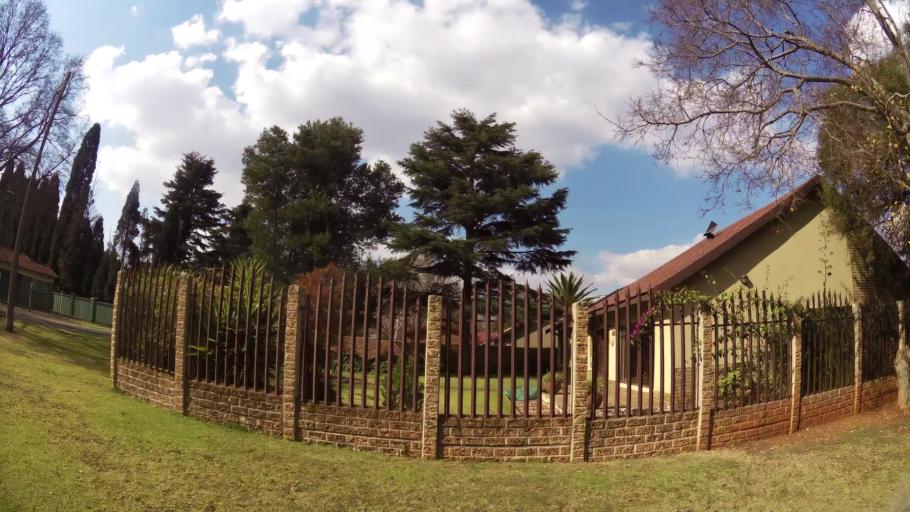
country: ZA
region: Mpumalanga
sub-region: Nkangala District Municipality
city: Delmas
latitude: -26.1408
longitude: 28.6750
